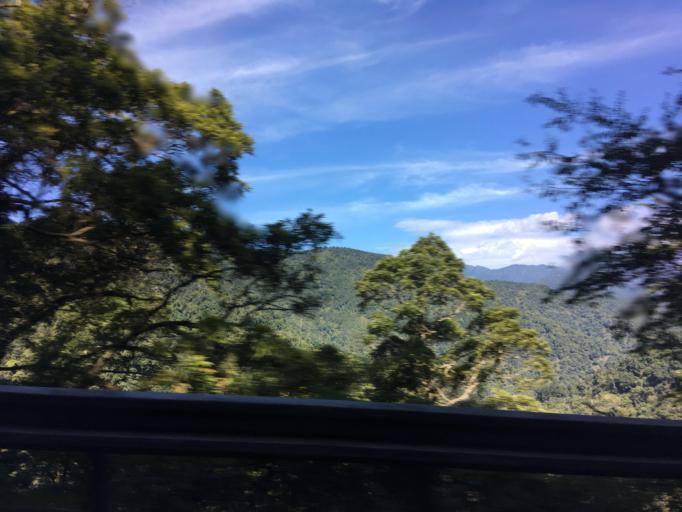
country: TW
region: Taiwan
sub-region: Yilan
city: Yilan
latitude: 24.5523
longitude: 121.5101
